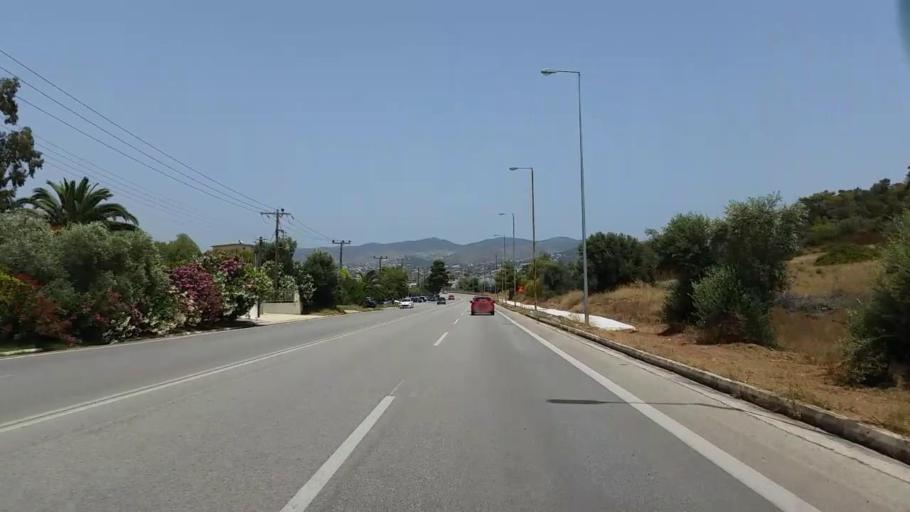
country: GR
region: Attica
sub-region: Nomarchia Anatolikis Attikis
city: Anavyssos
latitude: 37.7227
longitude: 23.9270
